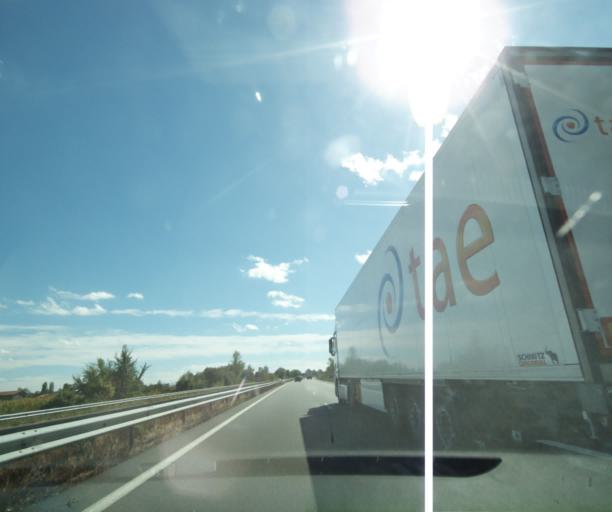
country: FR
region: Aquitaine
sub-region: Departement du Lot-et-Garonne
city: Damazan
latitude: 44.3241
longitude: 0.2589
